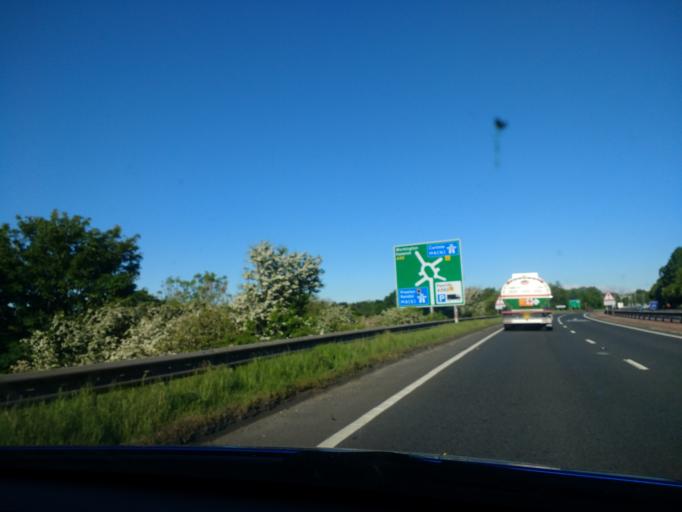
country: GB
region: England
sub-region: Cumbria
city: Penrith
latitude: 54.6500
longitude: -2.7535
